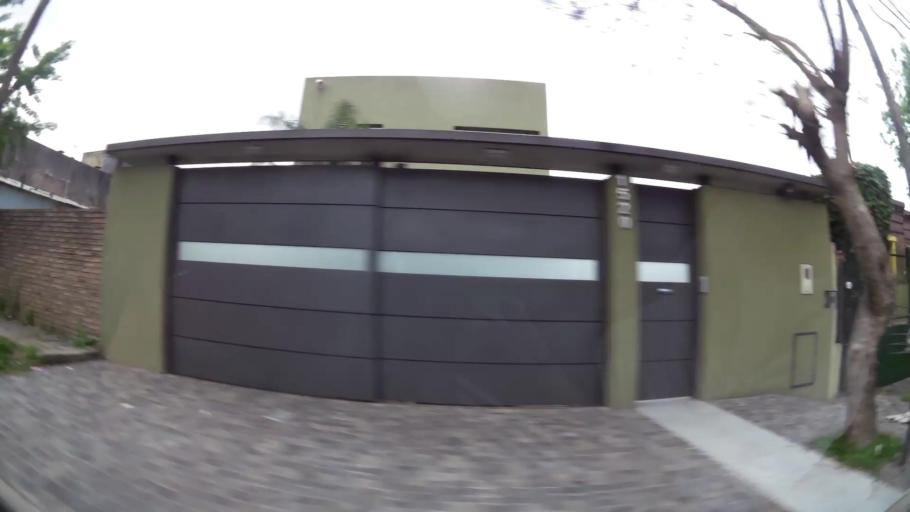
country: AR
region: Buenos Aires
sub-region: Partido de Quilmes
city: Quilmes
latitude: -34.7384
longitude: -58.2447
